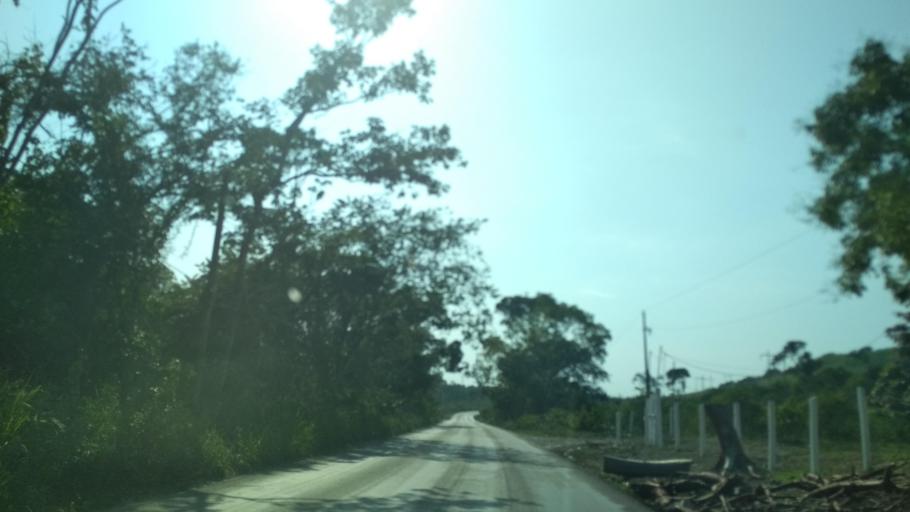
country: MM
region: Shan
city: Taunggyi
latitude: 20.3844
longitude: 97.2915
